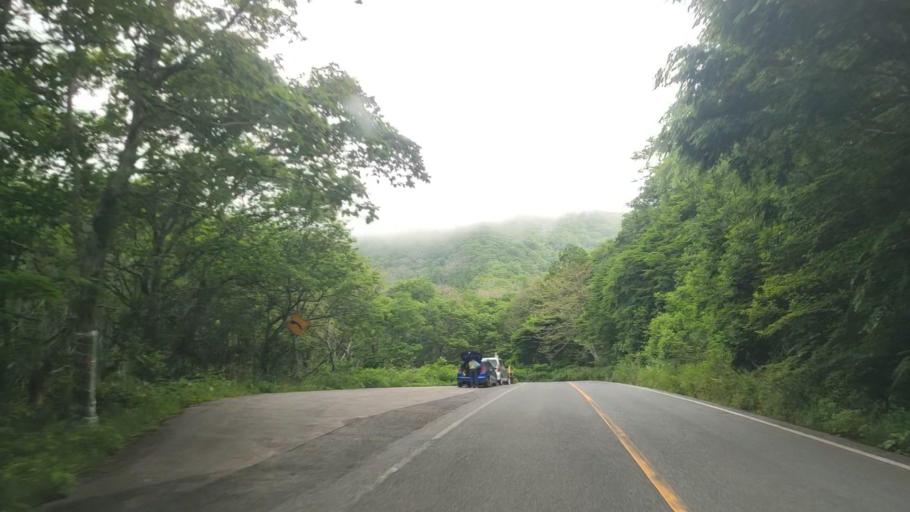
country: JP
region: Tottori
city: Yonago
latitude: 35.3325
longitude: 133.5725
